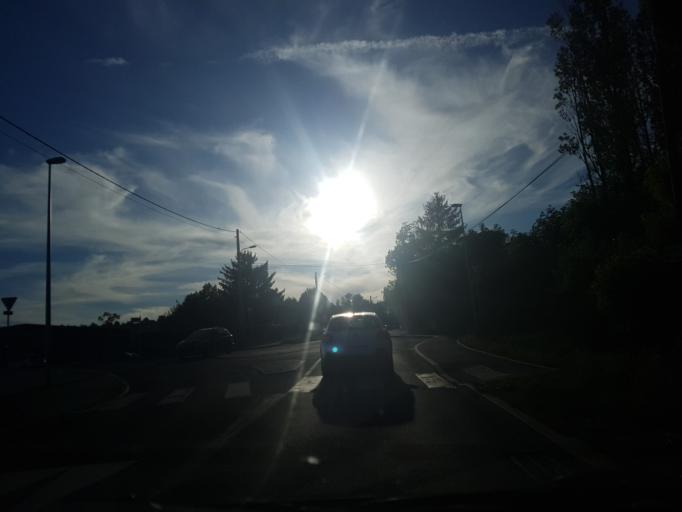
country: FR
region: Rhone-Alpes
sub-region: Departement du Rhone
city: Villefranche-sur-Saone
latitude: 45.9728
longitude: 4.7217
